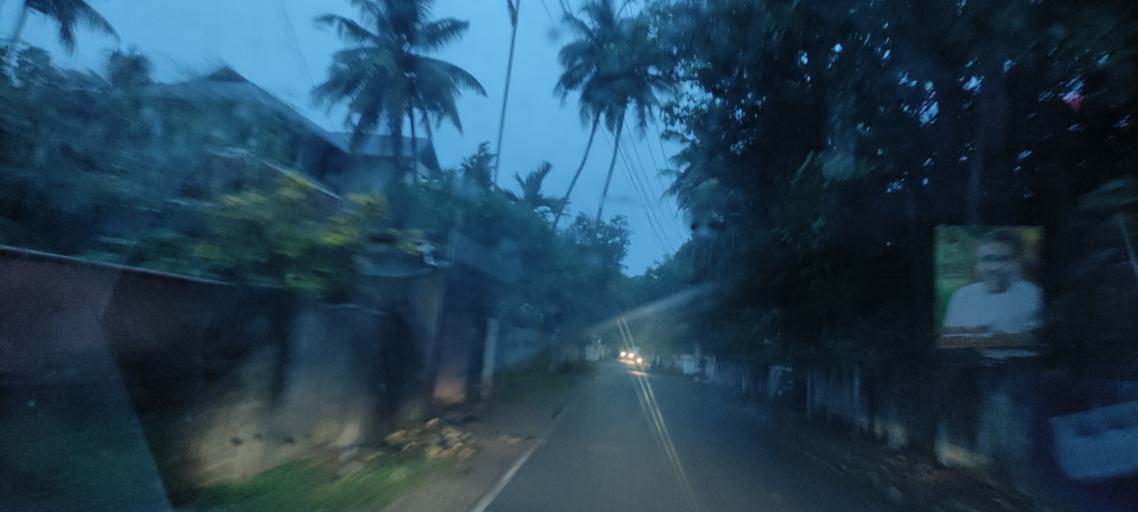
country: IN
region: Kerala
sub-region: Ernakulam
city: Cochin
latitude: 9.9167
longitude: 76.2908
